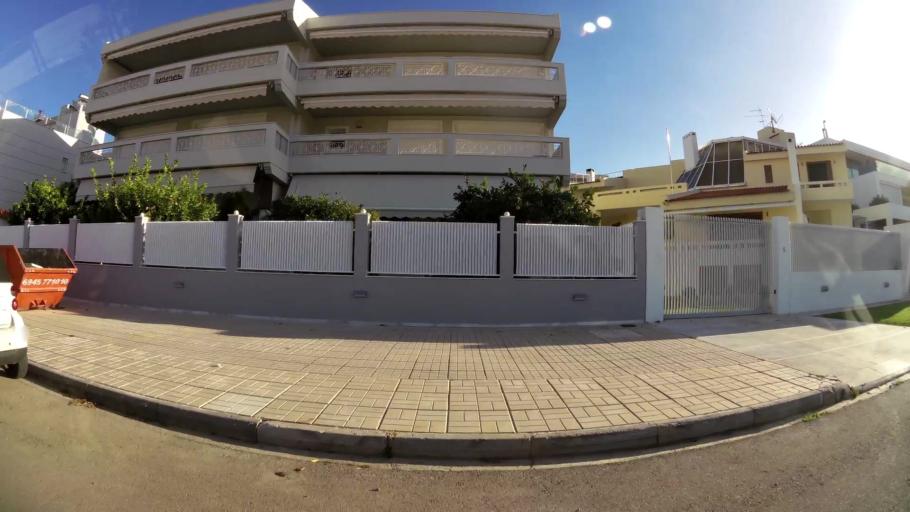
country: GR
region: Attica
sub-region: Nomarchia Athinas
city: Elliniko
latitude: 37.8824
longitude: 23.7421
